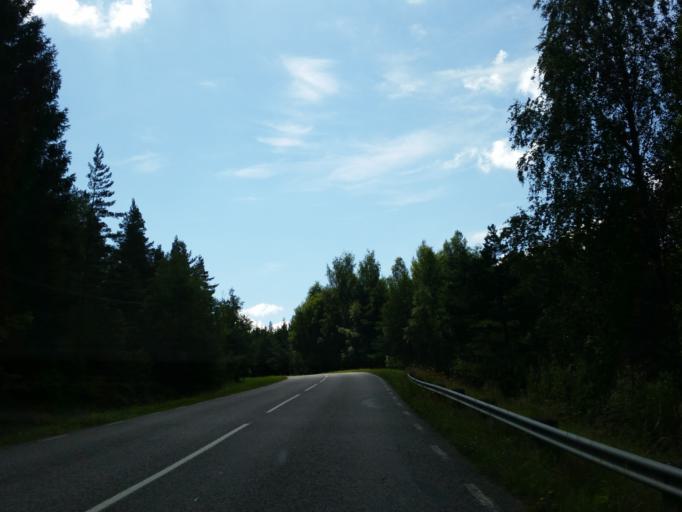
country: SE
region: Stockholm
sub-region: Sodertalje Kommun
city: Pershagen
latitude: 59.0123
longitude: 17.6636
